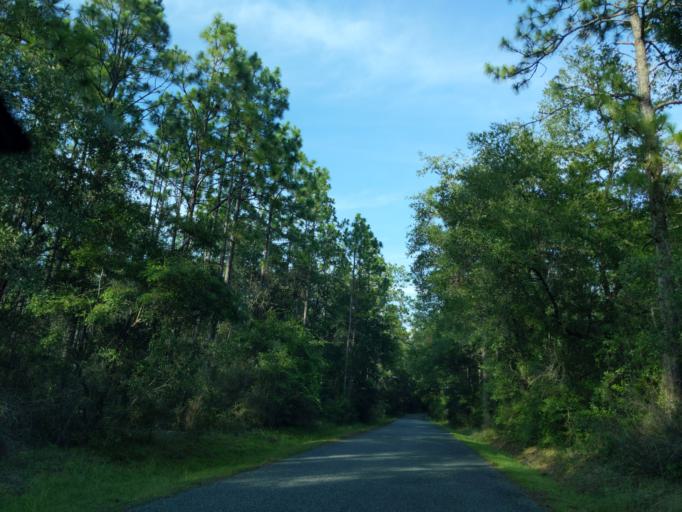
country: US
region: Florida
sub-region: Leon County
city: Woodville
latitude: 30.3477
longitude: -84.3690
